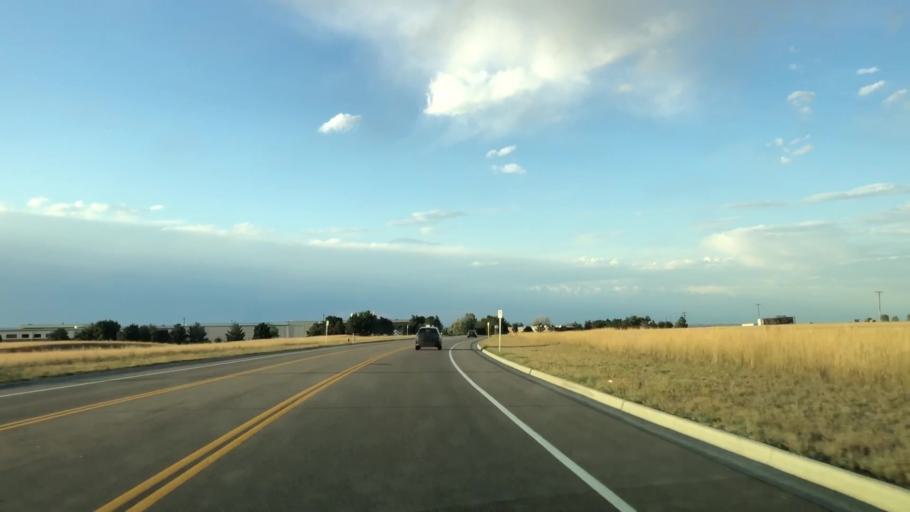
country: US
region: Colorado
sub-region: Larimer County
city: Loveland
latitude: 40.4464
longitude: -104.9946
